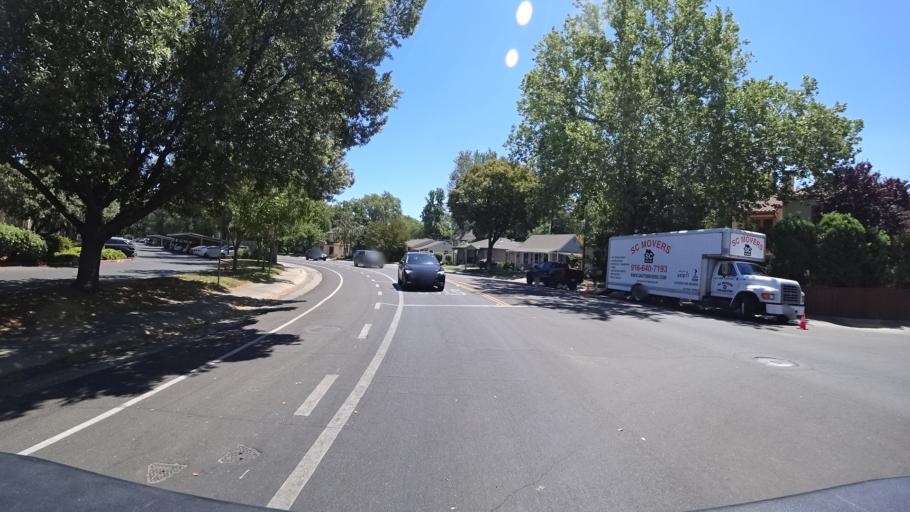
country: US
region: California
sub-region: Sacramento County
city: Sacramento
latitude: 38.5790
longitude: -121.4562
